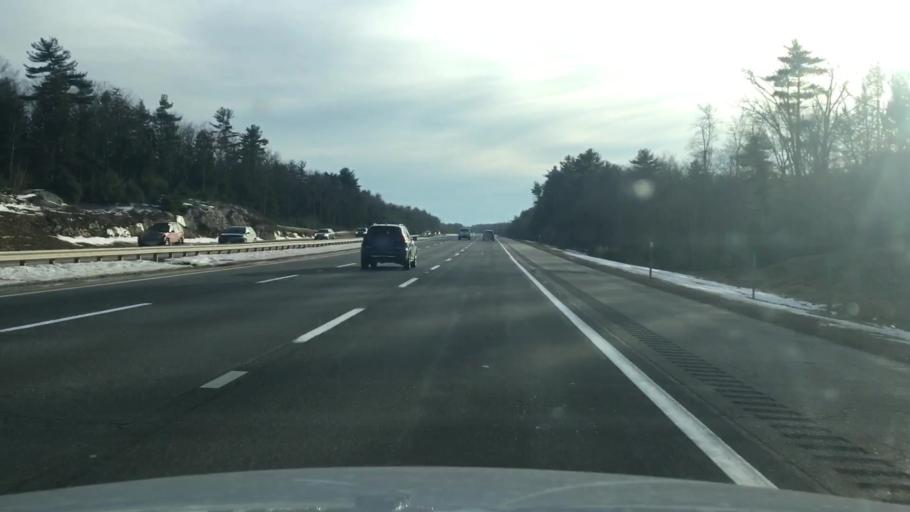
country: US
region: Maine
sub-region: York County
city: Ogunquit
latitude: 43.2485
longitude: -70.6257
